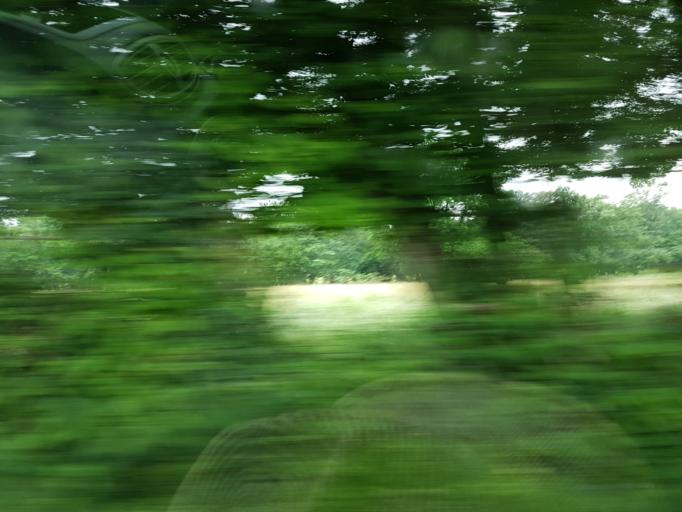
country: FR
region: Bourgogne
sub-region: Departement de la Nievre
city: Corbigny
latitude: 47.1840
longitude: 3.7362
